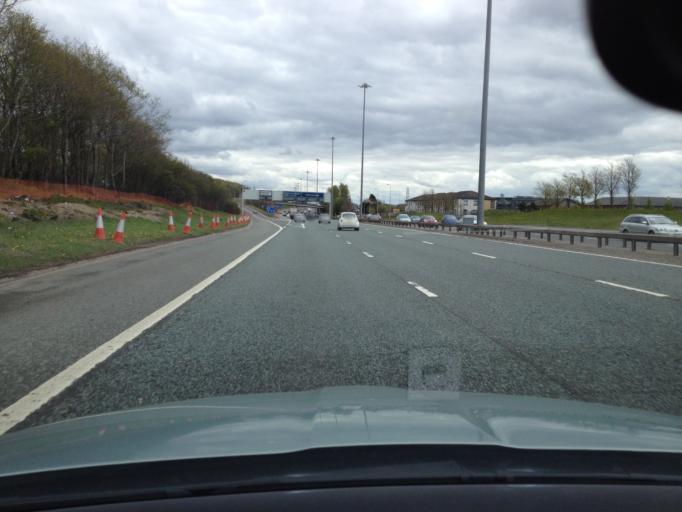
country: GB
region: Scotland
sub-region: North Lanarkshire
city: Chryston
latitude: 55.8629
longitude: -4.1169
